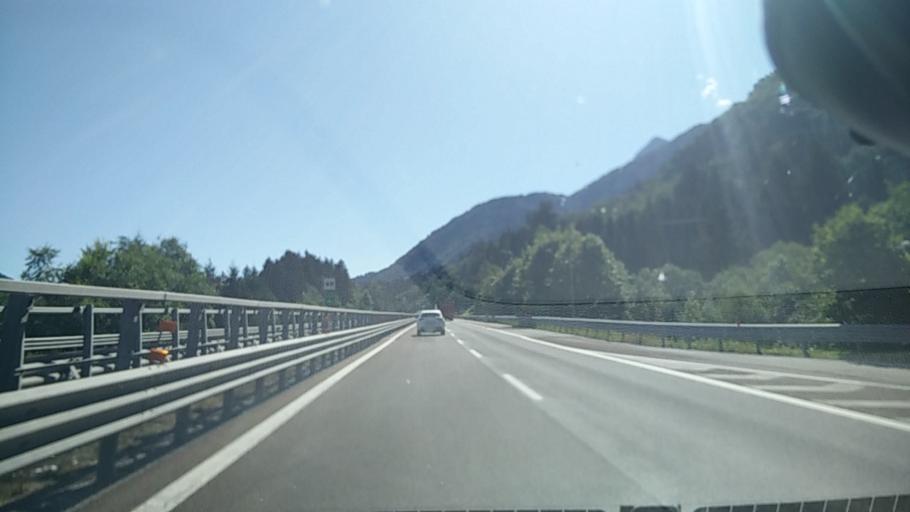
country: IT
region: Friuli Venezia Giulia
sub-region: Provincia di Udine
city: Malborghetto
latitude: 46.4983
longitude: 13.3900
